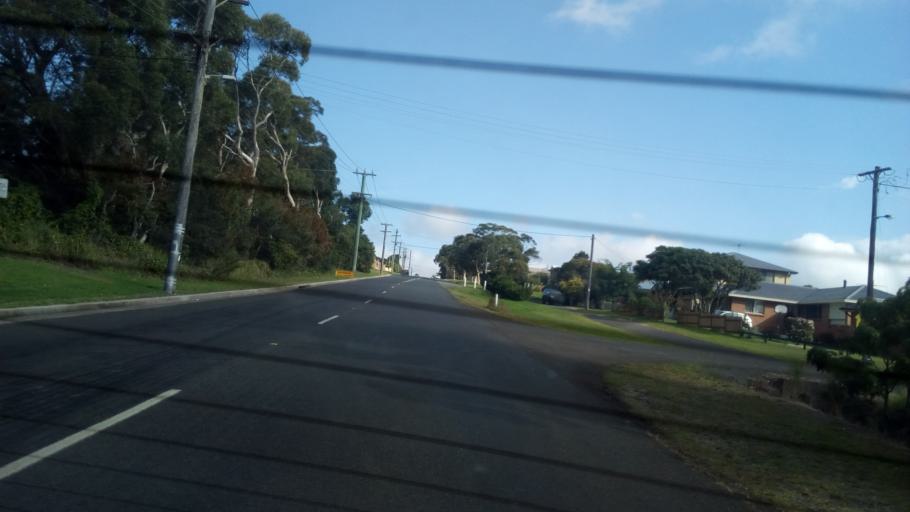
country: AU
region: New South Wales
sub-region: Wollongong
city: Helensburgh
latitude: -34.1981
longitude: 150.9806
